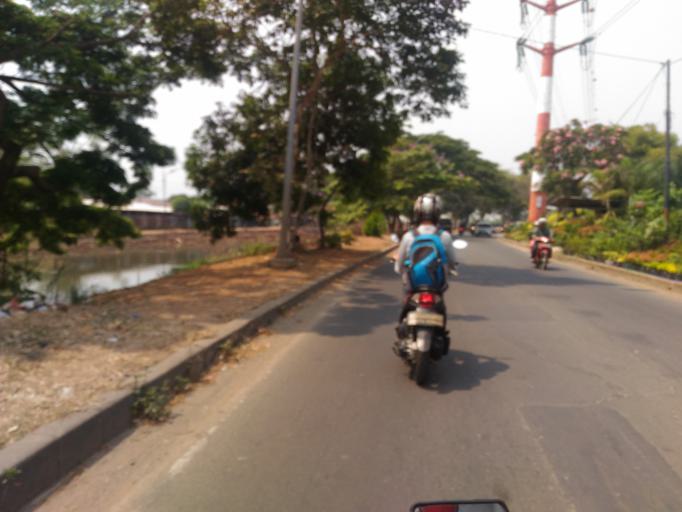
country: ID
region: West Java
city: Sepatan
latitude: -6.1491
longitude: 106.5999
